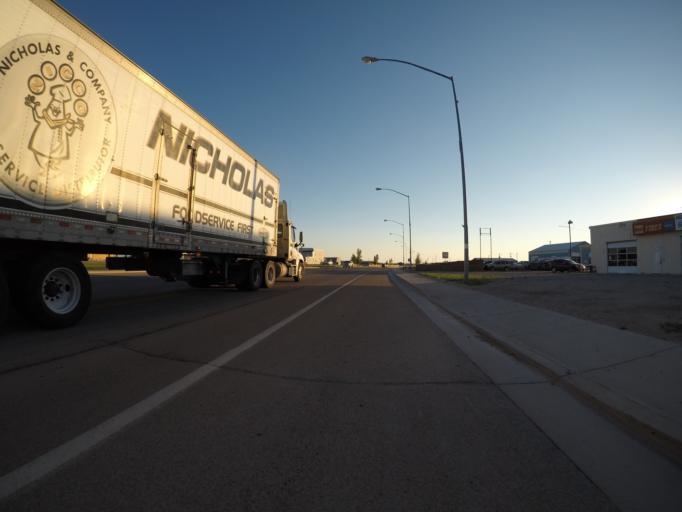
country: US
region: Wyoming
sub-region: Sublette County
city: Marbleton
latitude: 42.5558
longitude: -110.1093
